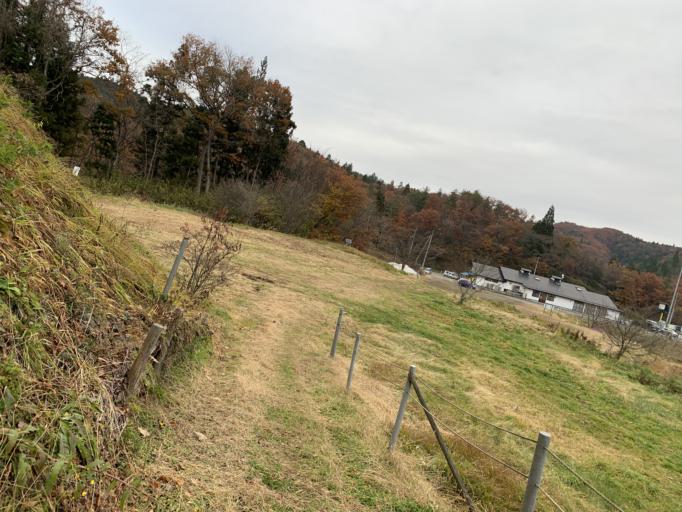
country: JP
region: Iwate
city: Kitakami
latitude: 39.2984
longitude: 141.2044
